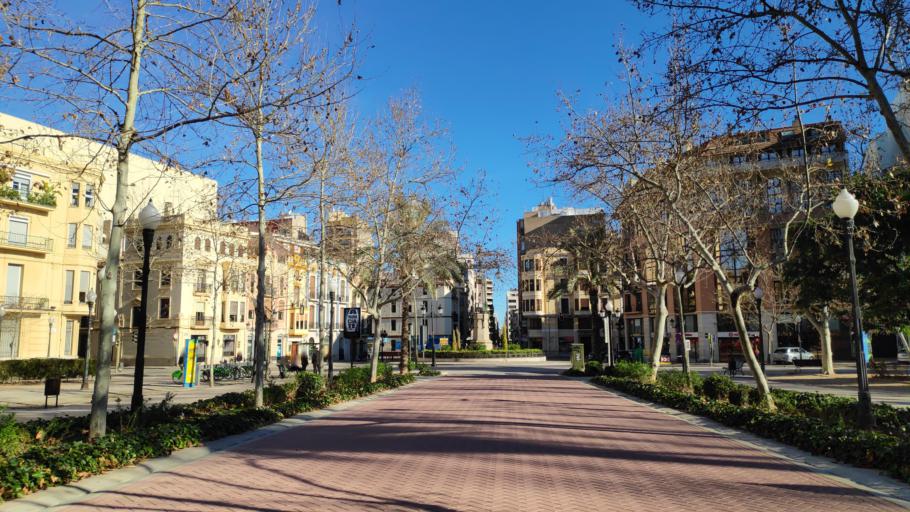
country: ES
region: Valencia
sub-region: Provincia de Castello
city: Castello de la Plana
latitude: 39.9879
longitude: -0.0435
